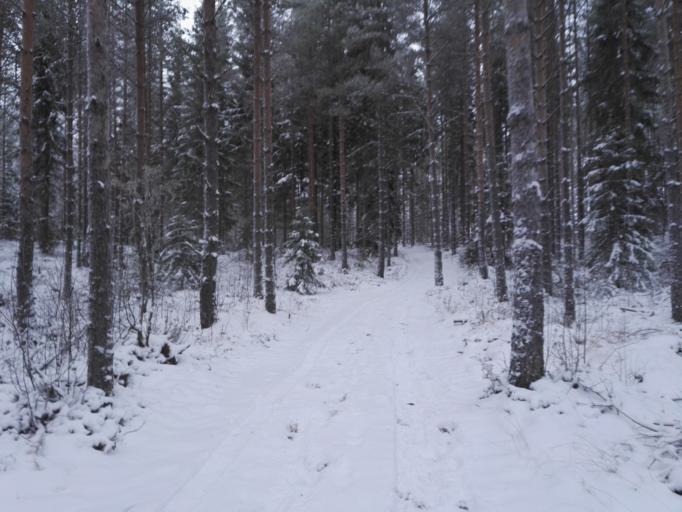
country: FI
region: Satakunta
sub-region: Pohjois-Satakunta
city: Jaemijaervi
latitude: 61.7826
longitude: 22.8705
